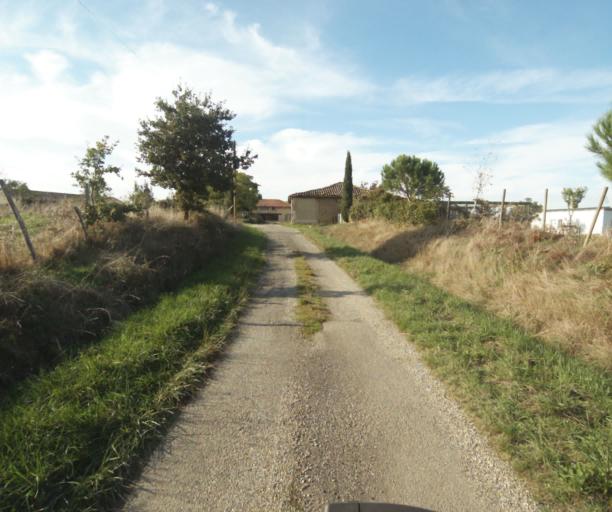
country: FR
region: Midi-Pyrenees
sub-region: Departement du Tarn-et-Garonne
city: Saint-Porquier
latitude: 43.9191
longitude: 1.1149
